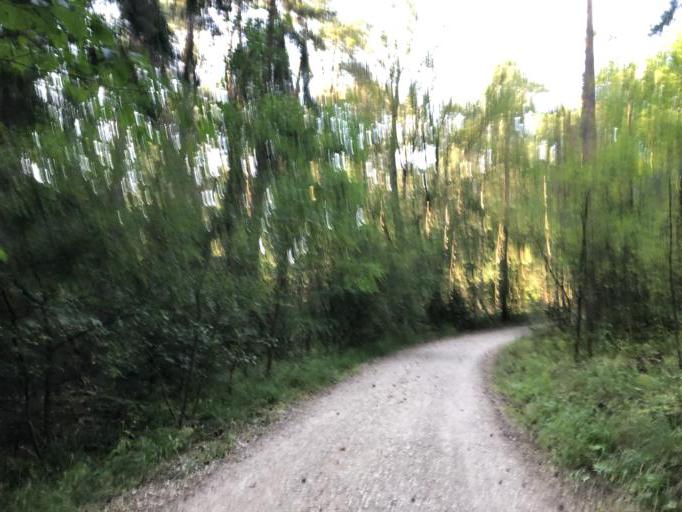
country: DE
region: Bavaria
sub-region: Regierungsbezirk Mittelfranken
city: Kalchreuth
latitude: 49.5521
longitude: 11.1042
